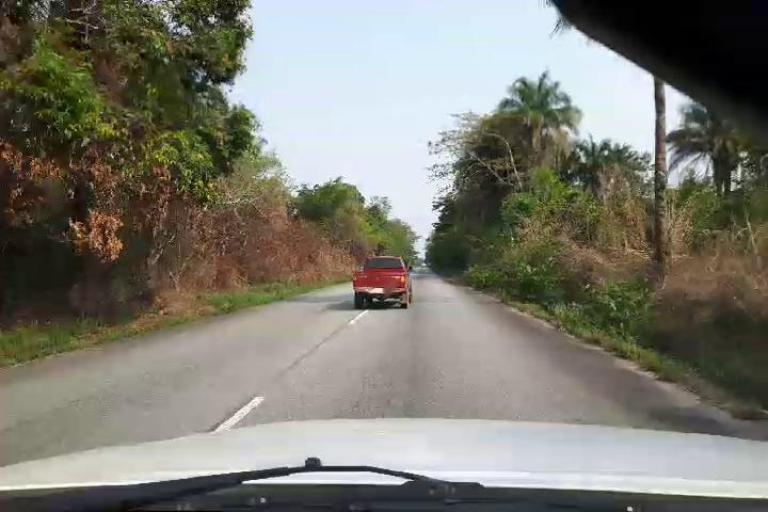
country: SL
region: Southern Province
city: Baiima
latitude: 8.1360
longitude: -11.8923
